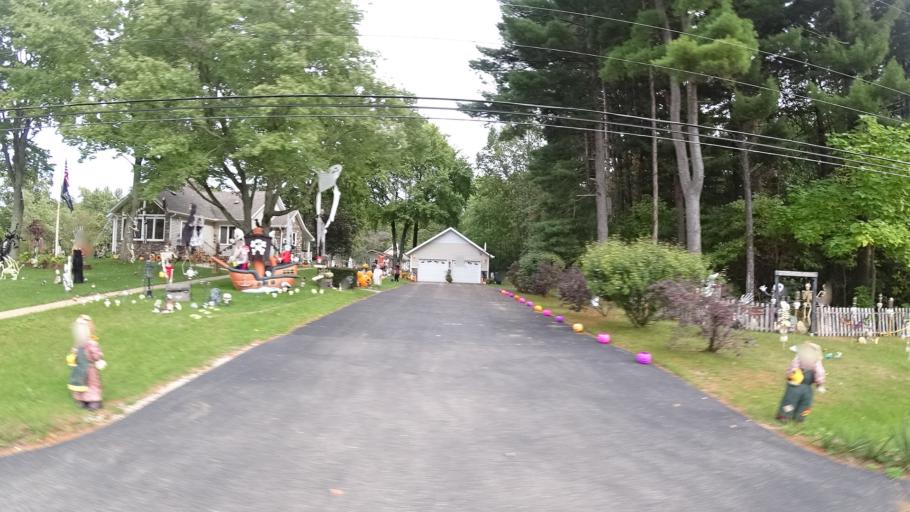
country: US
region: Indiana
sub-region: LaPorte County
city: Long Beach
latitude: 41.7194
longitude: -86.8162
